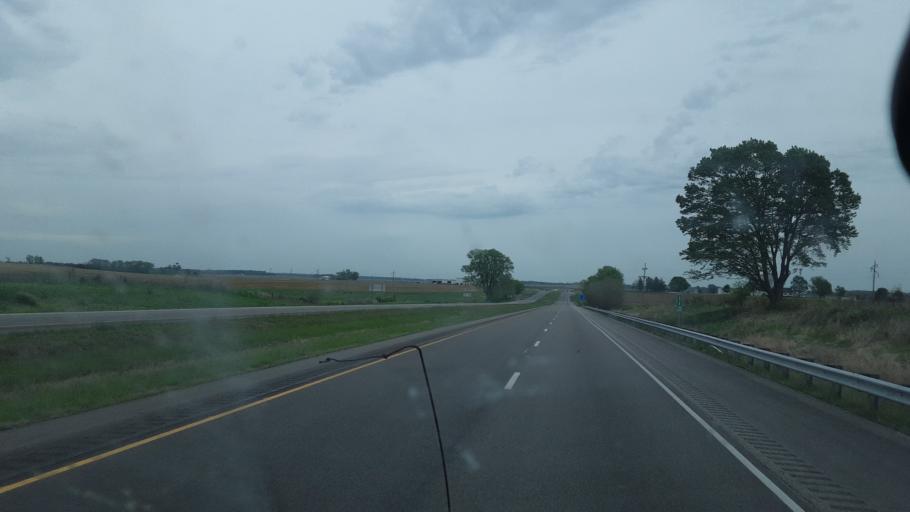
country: US
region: Indiana
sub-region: Posey County
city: Poseyville
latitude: 38.1841
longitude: -87.7972
